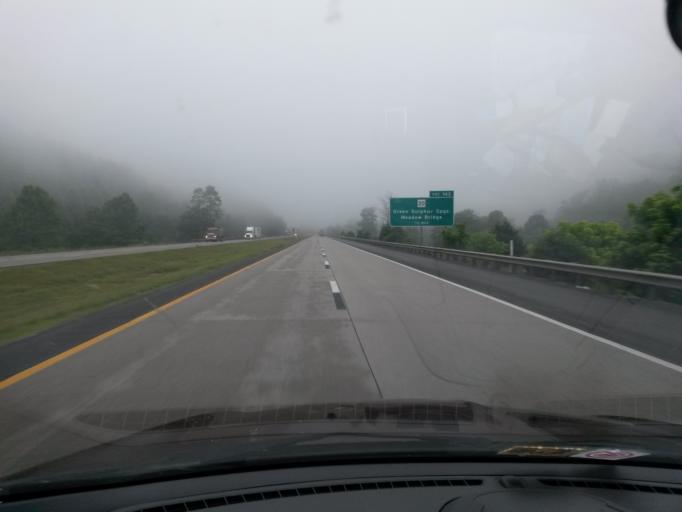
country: US
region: West Virginia
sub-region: Greenbrier County
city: Rainelle
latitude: 37.8163
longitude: -80.8136
